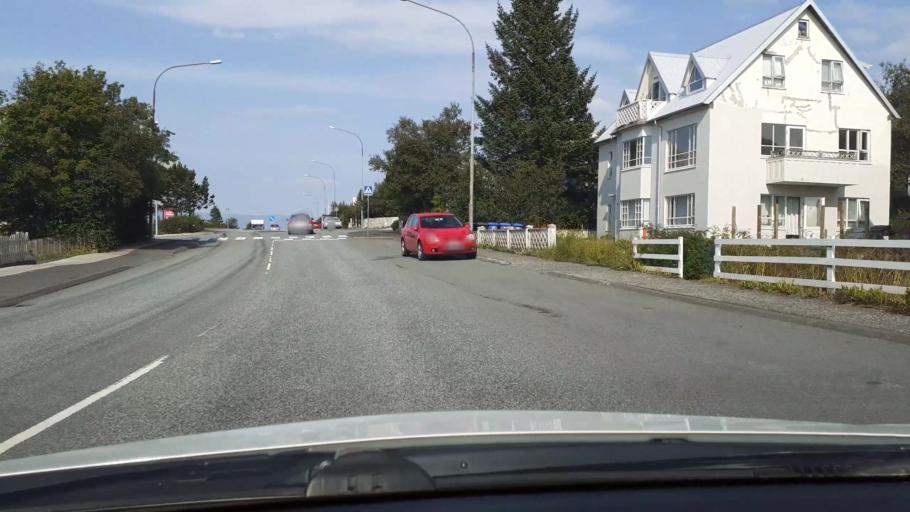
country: IS
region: Capital Region
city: Hafnarfjoerdur
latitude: 64.0636
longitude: -21.9495
